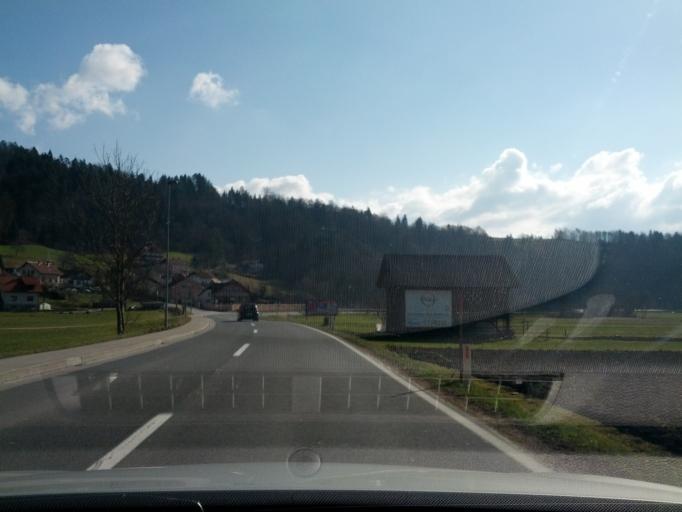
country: SI
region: Litija
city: Litija
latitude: 46.0917
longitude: 14.8302
